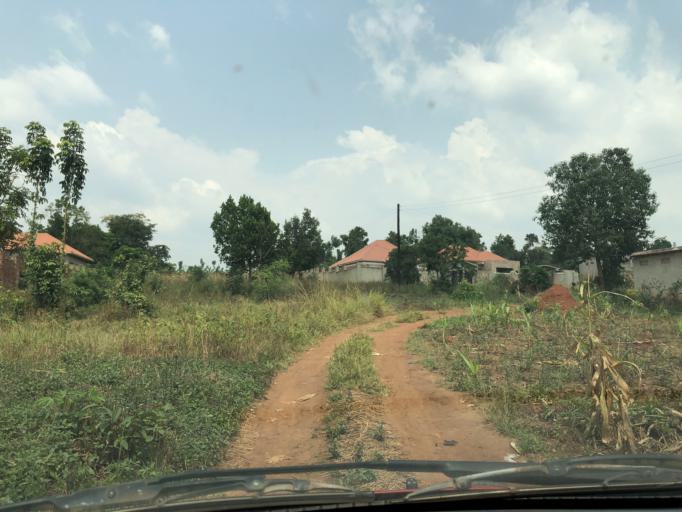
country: UG
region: Central Region
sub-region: Wakiso District
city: Bweyogerere
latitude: 0.4746
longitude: 32.6372
